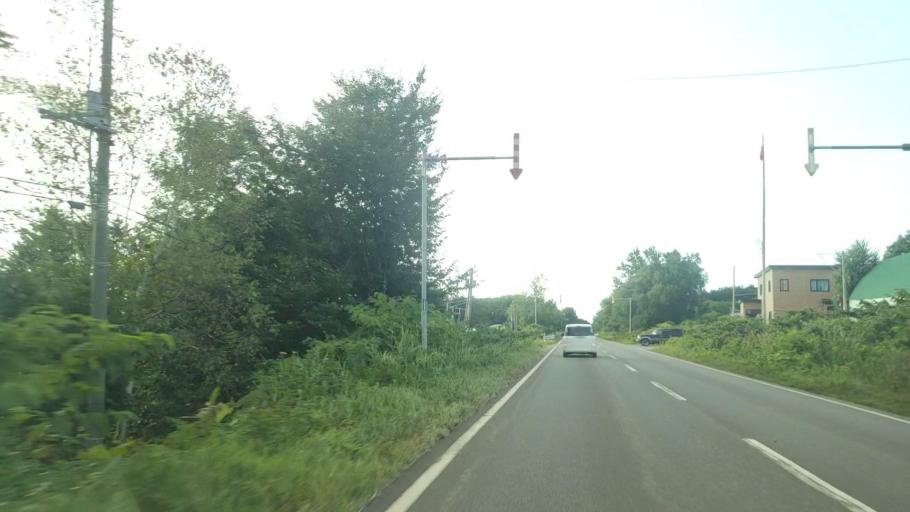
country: JP
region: Hokkaido
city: Makubetsu
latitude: 45.0446
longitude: 141.7540
